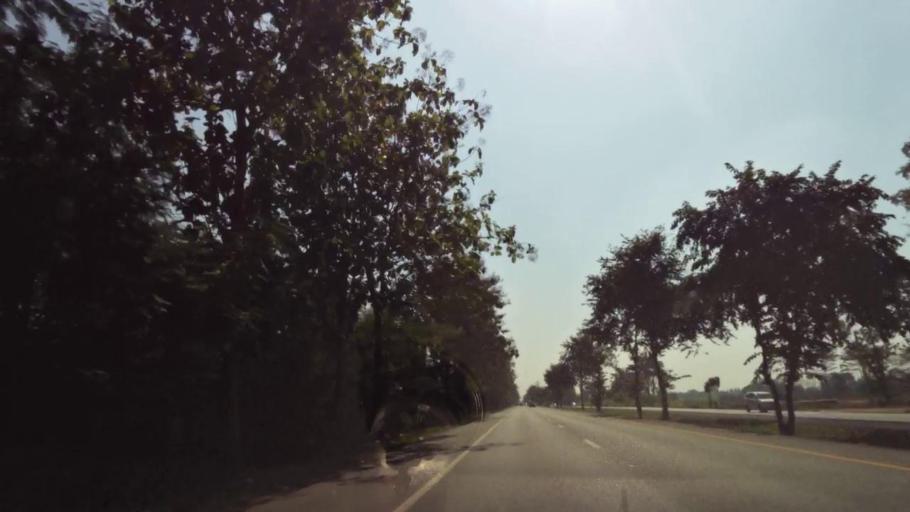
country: TH
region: Phichit
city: Bueng Na Rang
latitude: 16.0877
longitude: 100.1250
